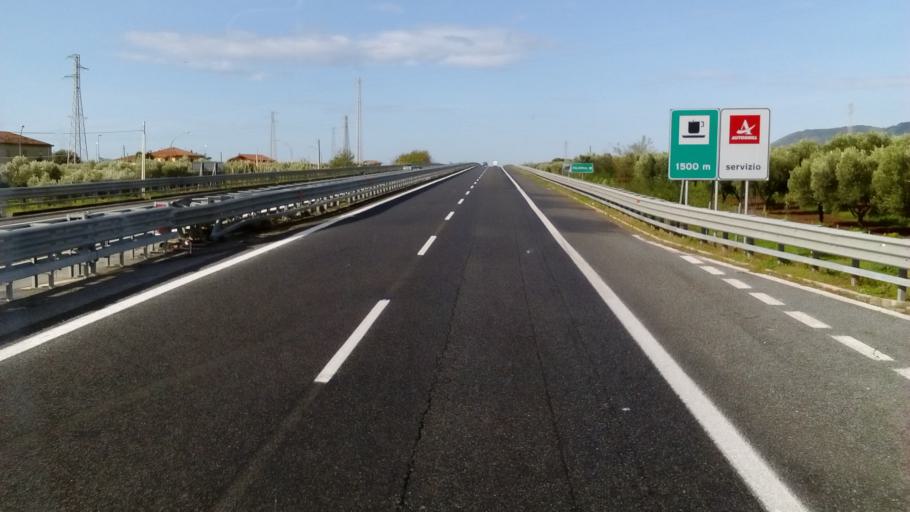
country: IT
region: Calabria
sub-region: Provincia di Catanzaro
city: Santa Eufemia Lamezia
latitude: 38.9248
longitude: 16.2552
